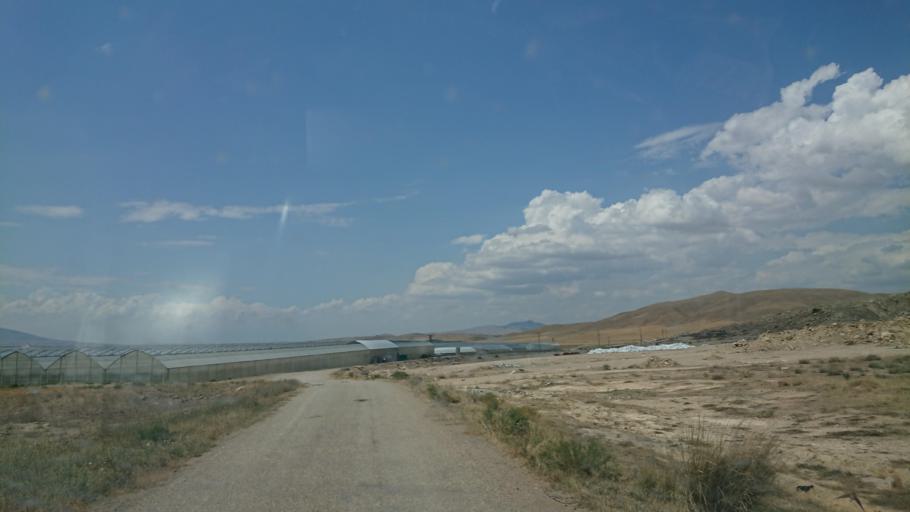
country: TR
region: Aksaray
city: Sariyahsi
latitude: 38.9973
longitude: 33.9140
